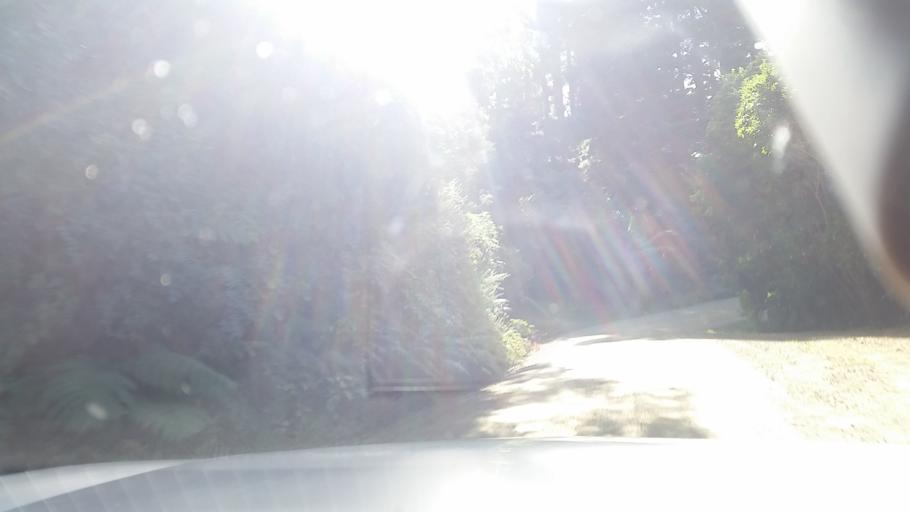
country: NZ
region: Marlborough
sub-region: Marlborough District
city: Picton
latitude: -41.2880
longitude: 174.1737
